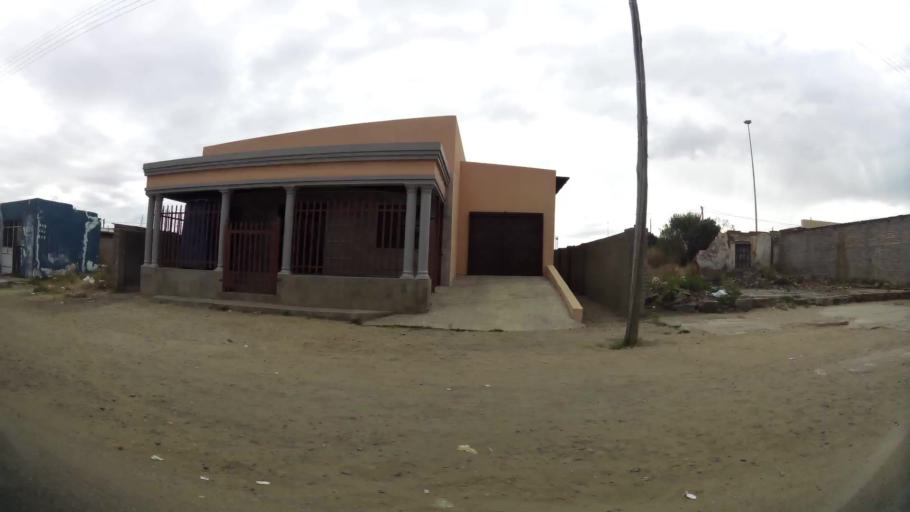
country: ZA
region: Orange Free State
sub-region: Fezile Dabi District Municipality
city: Kroonstad
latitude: -27.6507
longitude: 27.2081
